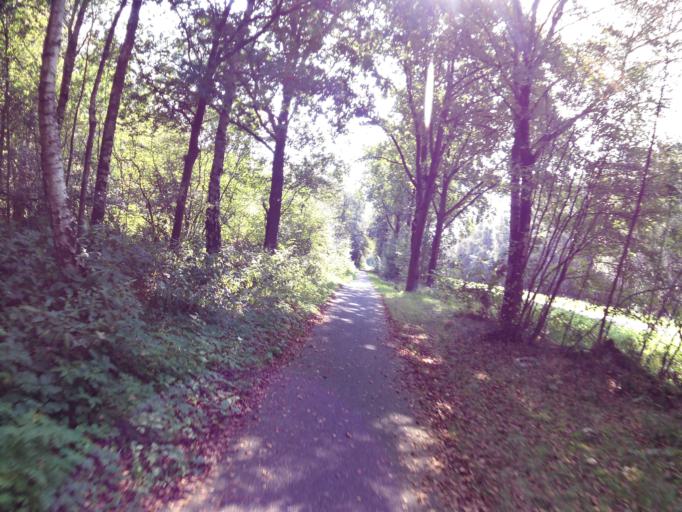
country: NL
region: Overijssel
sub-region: Gemeente Twenterand
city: Westerhaar-Vriezenveensewijk
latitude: 52.4714
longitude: 6.6509
